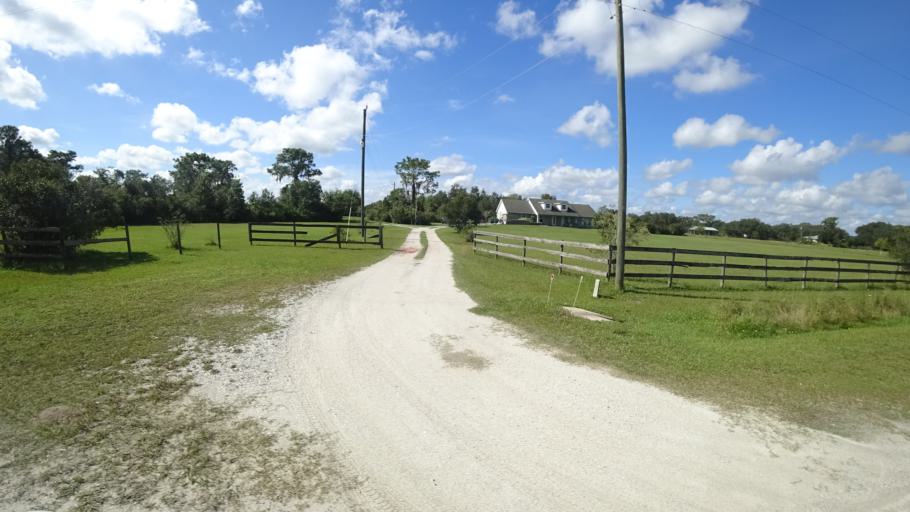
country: US
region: Florida
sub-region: DeSoto County
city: Arcadia
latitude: 27.3589
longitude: -82.1310
